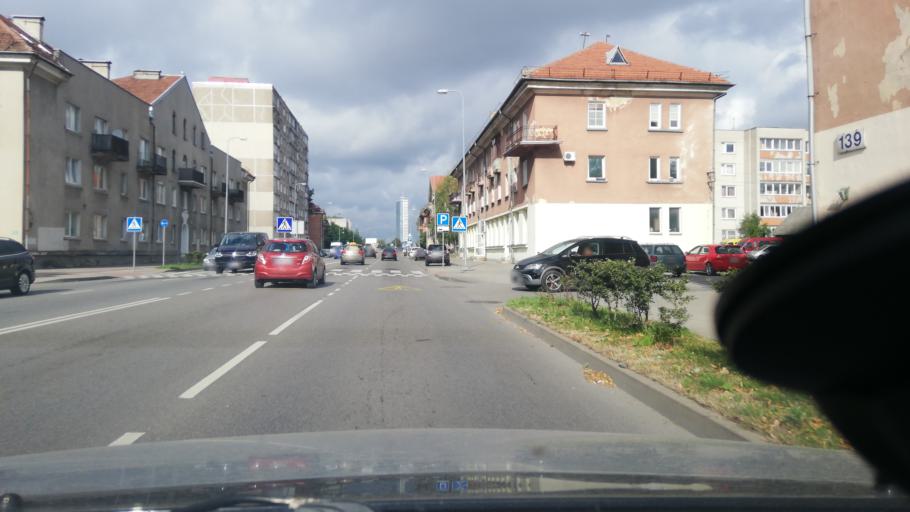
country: LT
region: Klaipedos apskritis
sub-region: Klaipeda
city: Klaipeda
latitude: 55.6787
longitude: 21.1522
